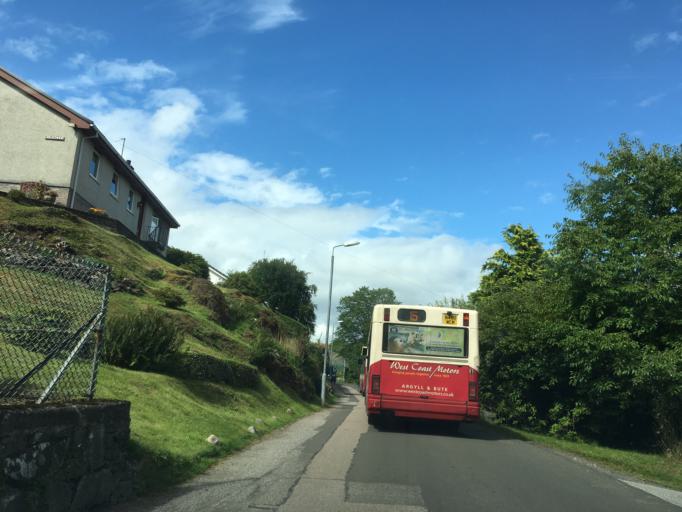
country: GB
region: Scotland
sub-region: Argyll and Bute
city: Oban
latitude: 56.4532
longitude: -5.3859
